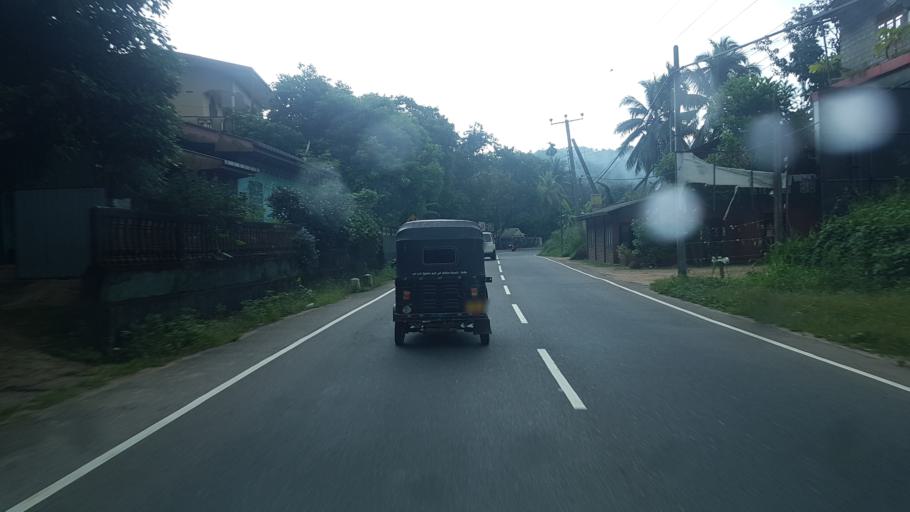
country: LK
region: Western
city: Hanwella Ihala
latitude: 6.9632
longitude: 80.2296
